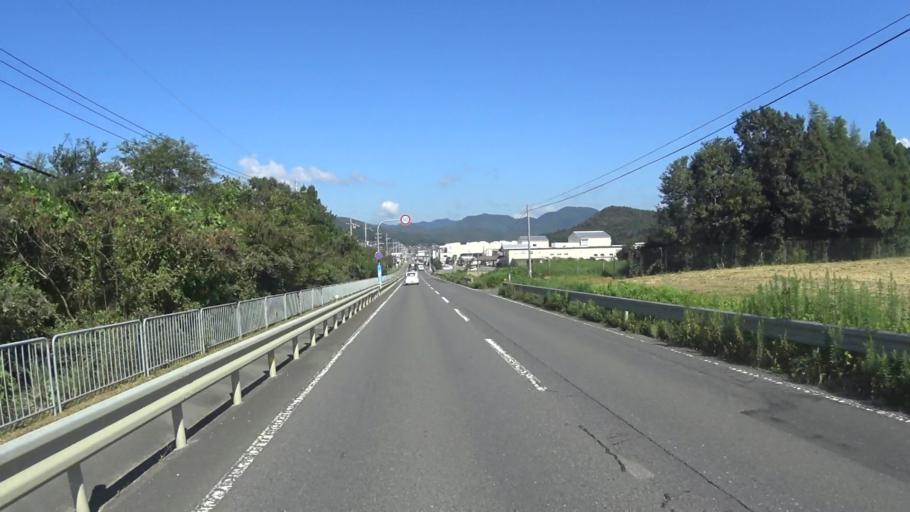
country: JP
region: Kyoto
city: Ayabe
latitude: 35.1750
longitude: 135.4235
